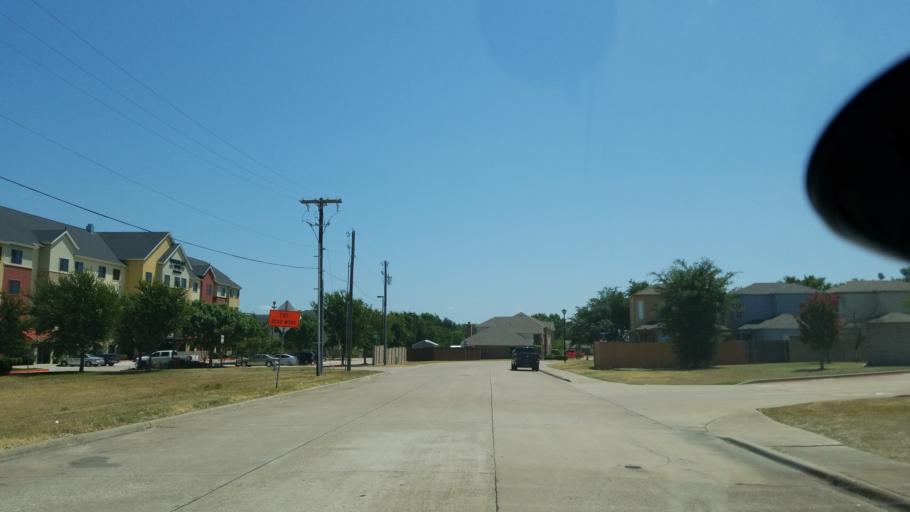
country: US
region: Texas
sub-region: Dallas County
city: Duncanville
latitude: 32.6457
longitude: -96.8856
